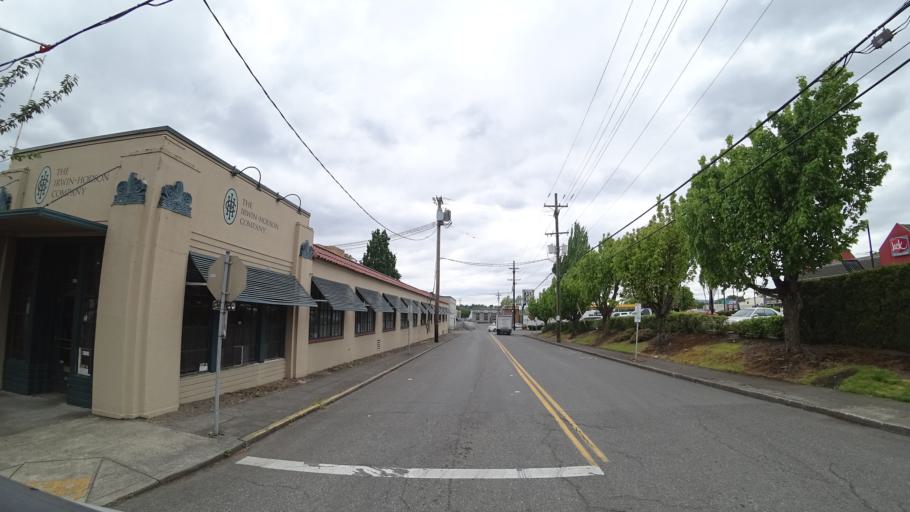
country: US
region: Oregon
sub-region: Multnomah County
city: Portland
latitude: 45.5021
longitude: -122.6567
